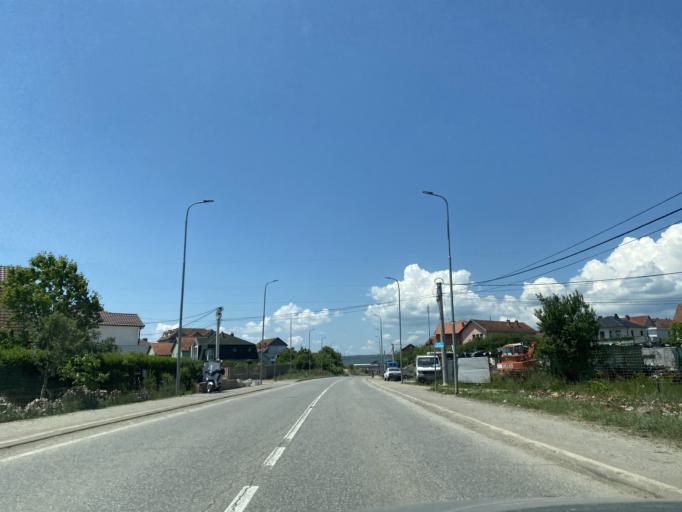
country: XK
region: Pristina
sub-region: Podujevo
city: Podujeva
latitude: 42.9004
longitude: 21.2089
